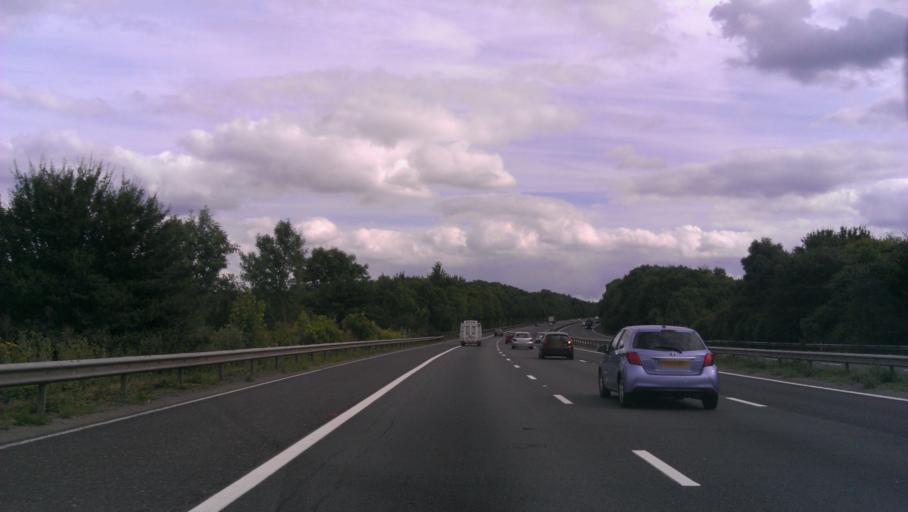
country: GB
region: England
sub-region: Kent
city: Longfield
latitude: 51.3624
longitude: 0.2666
